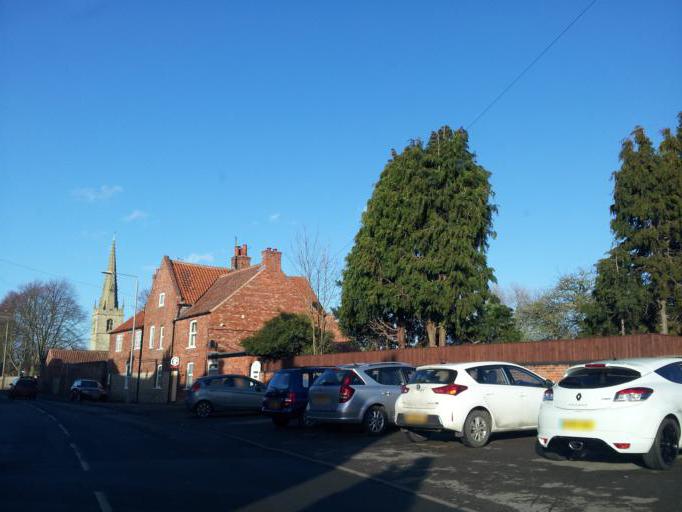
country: GB
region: England
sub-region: Nottinghamshire
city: Newark on Trent
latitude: 53.0539
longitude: -0.7789
